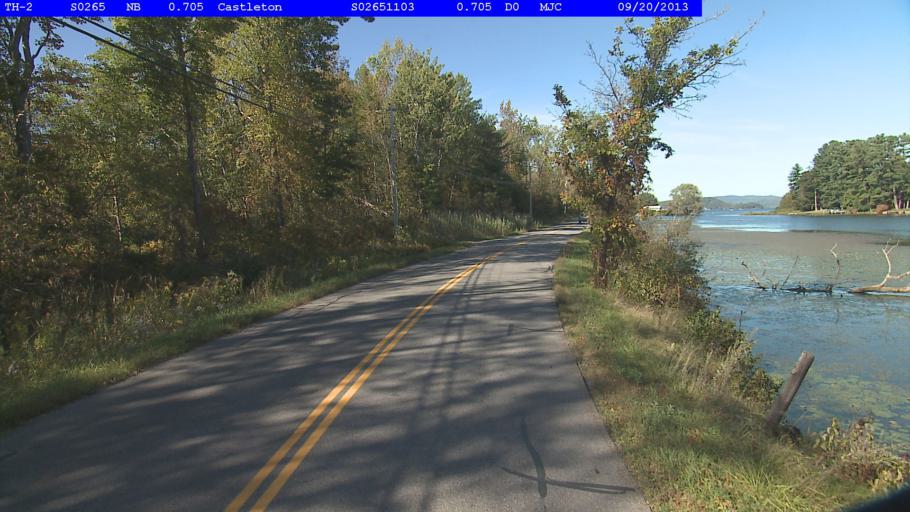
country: US
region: Vermont
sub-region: Rutland County
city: Fair Haven
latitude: 43.6144
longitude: -73.2317
